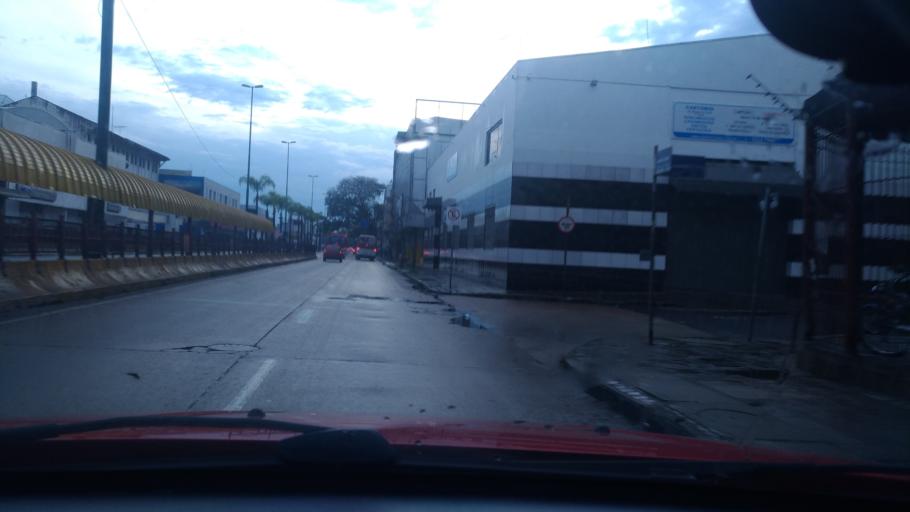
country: BR
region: Rio Grande do Sul
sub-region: Porto Alegre
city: Porto Alegre
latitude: -30.0241
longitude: -51.2140
